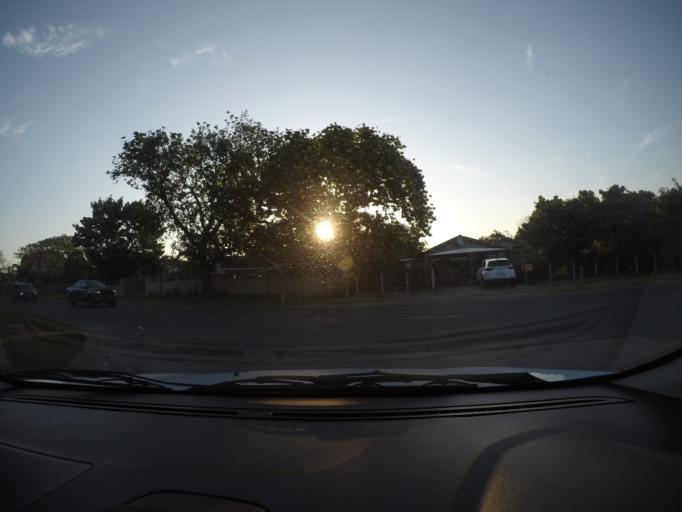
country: ZA
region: KwaZulu-Natal
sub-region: uThungulu District Municipality
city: Richards Bay
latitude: -28.7811
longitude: 32.0997
